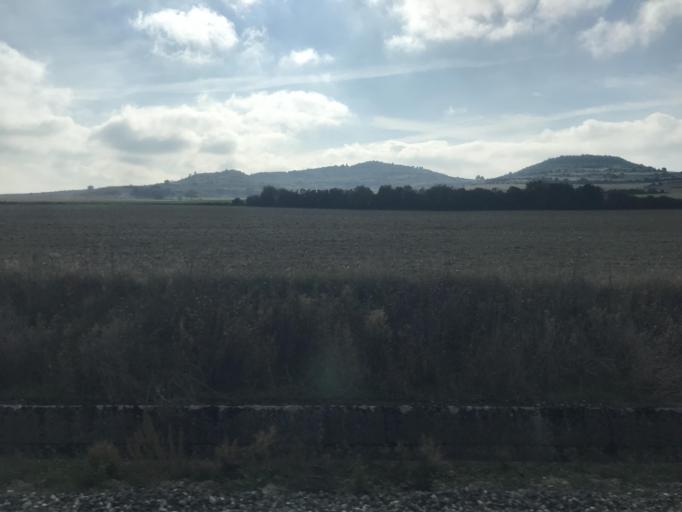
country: ES
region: Basque Country
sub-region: Provincia de Alava
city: Gasteiz / Vitoria
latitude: 42.8426
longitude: -2.7685
